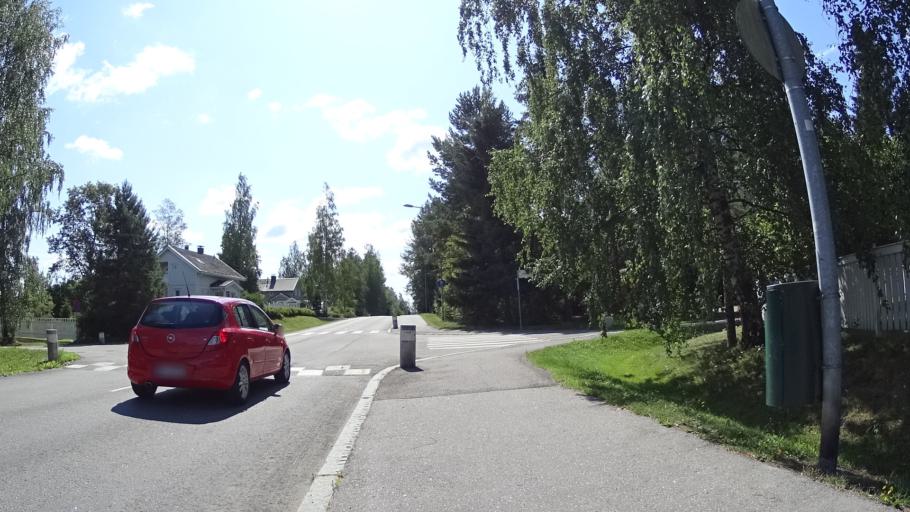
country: FI
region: Uusimaa
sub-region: Helsinki
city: Jaervenpaeae
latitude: 60.4851
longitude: 25.0658
